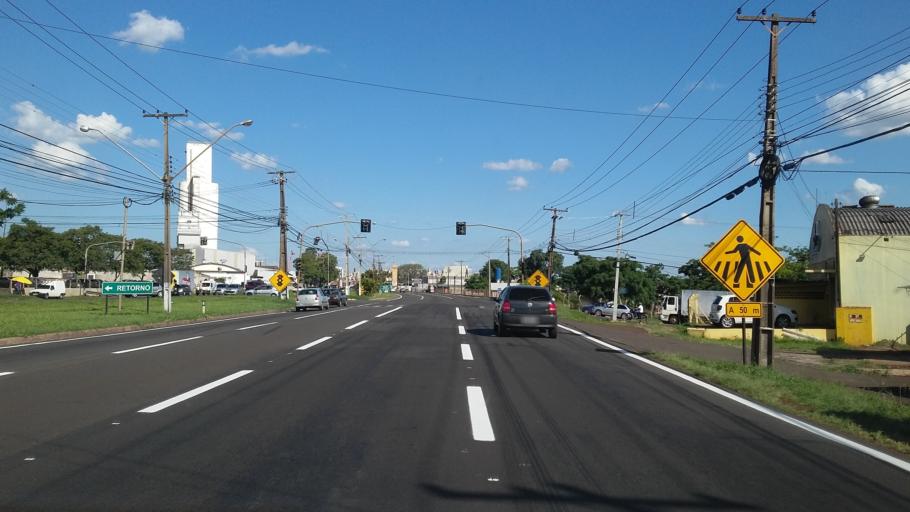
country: BR
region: Parana
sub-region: Londrina
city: Londrina
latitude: -23.2952
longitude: -51.2095
